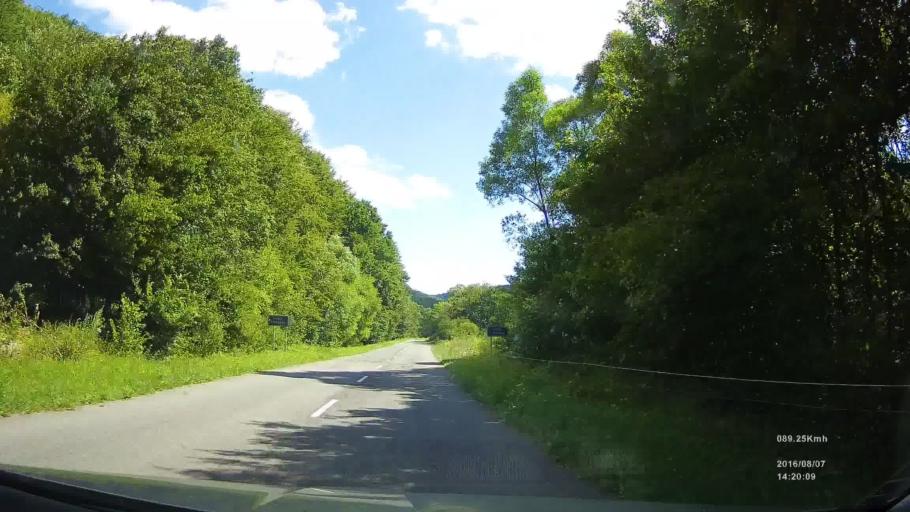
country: SK
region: Presovsky
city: Stropkov
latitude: 49.2940
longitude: 21.7593
